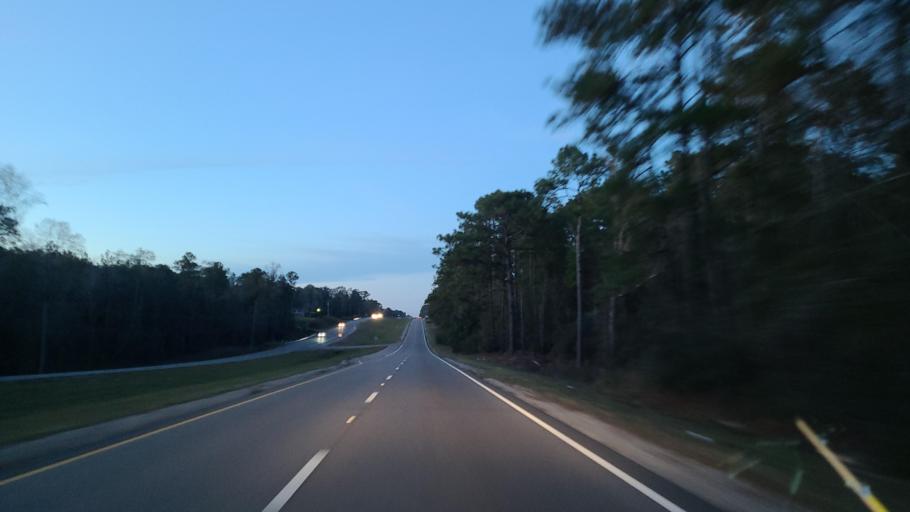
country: US
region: Mississippi
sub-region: Forrest County
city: Hattiesburg
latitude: 31.1962
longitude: -89.2553
